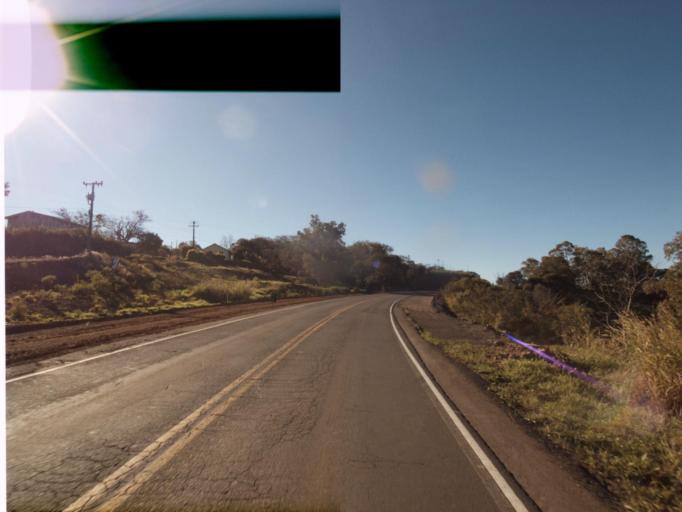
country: AR
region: Misiones
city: Bernardo de Irigoyen
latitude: -26.6943
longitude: -53.5160
